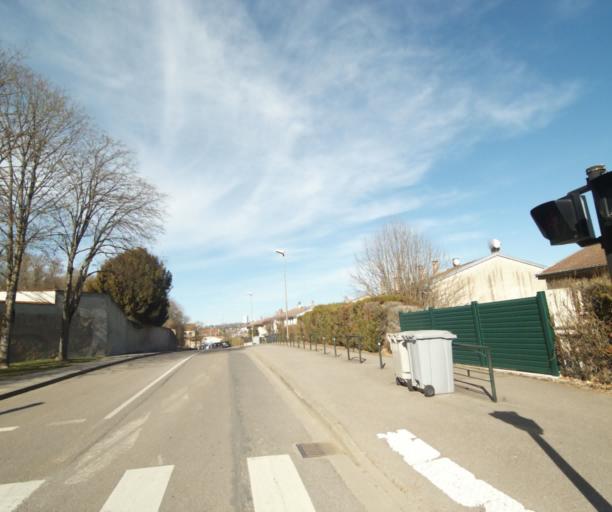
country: FR
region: Lorraine
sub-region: Departement de Meurthe-et-Moselle
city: Villers-les-Nancy
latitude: 48.6709
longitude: 6.1479
